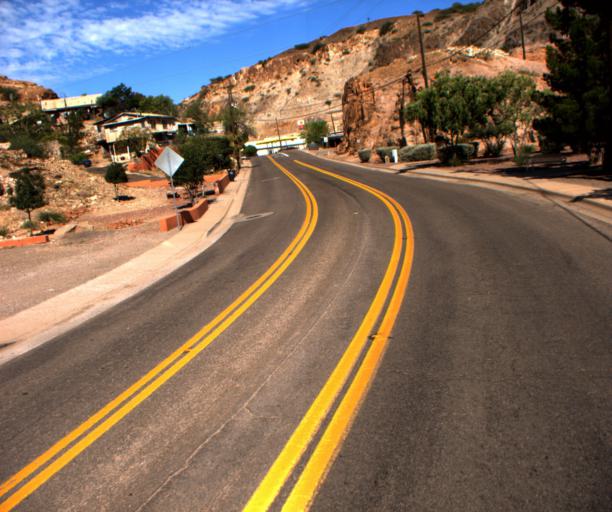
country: US
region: Arizona
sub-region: Greenlee County
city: Clifton
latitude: 33.0562
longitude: -109.3000
